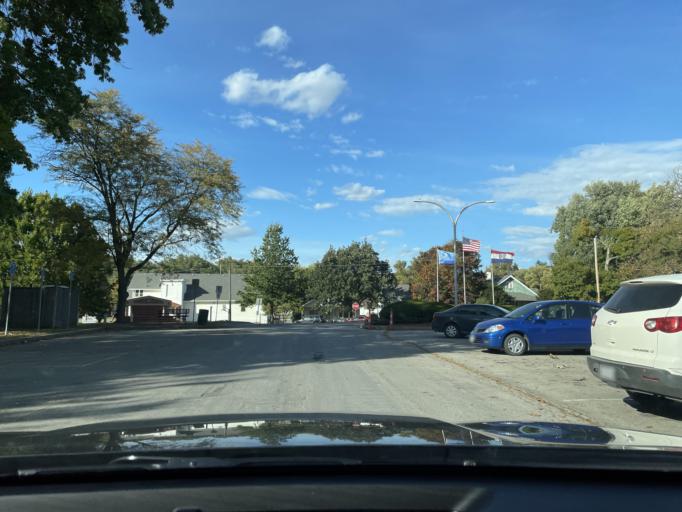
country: US
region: Kansas
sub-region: Doniphan County
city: Elwood
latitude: 39.7107
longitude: -94.8505
